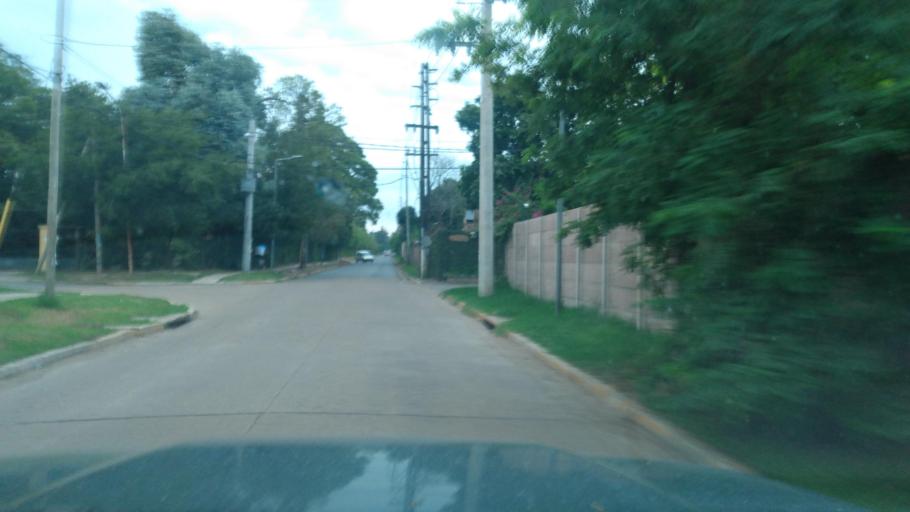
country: AR
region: Buenos Aires
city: Hurlingham
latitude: -34.5691
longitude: -58.7118
